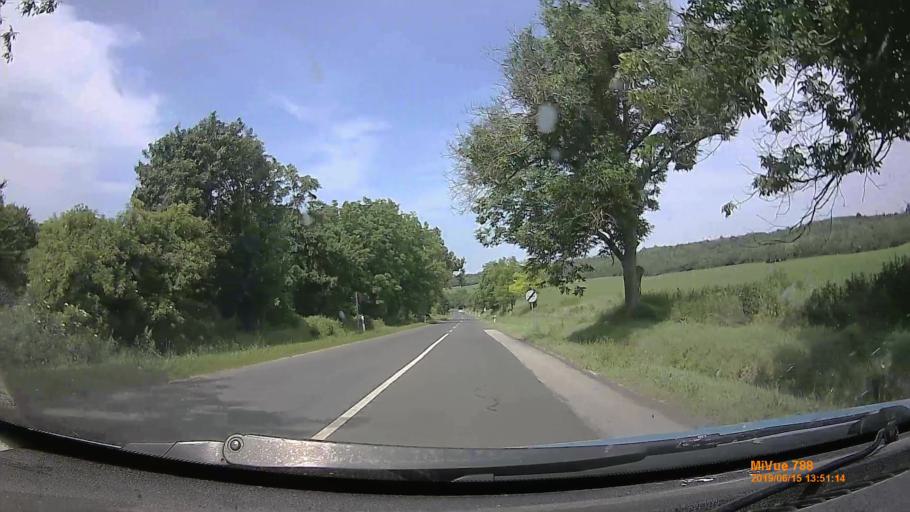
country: HU
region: Tolna
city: Iregszemcse
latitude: 46.7514
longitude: 18.1658
